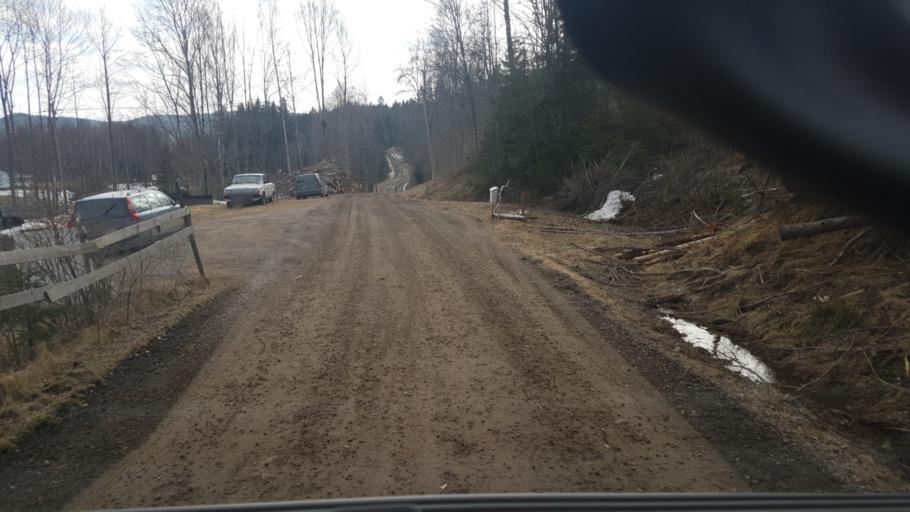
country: SE
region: Vaermland
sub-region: Eda Kommun
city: Amotfors
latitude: 59.8162
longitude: 12.4196
